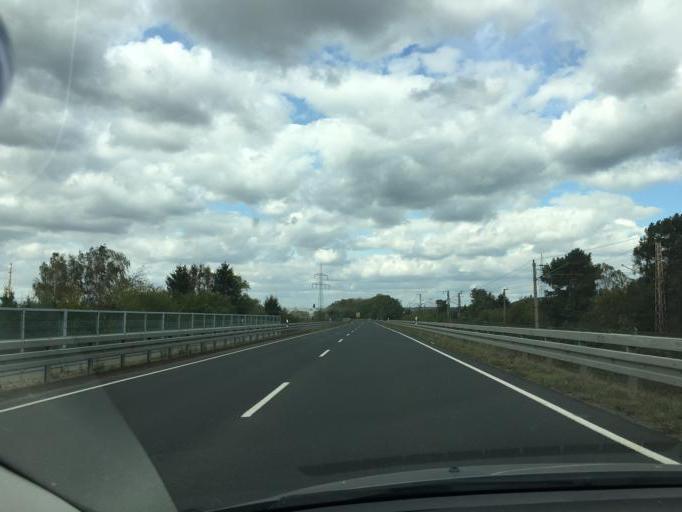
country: DE
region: Saxony
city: Coswig
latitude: 51.0997
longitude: 13.6034
